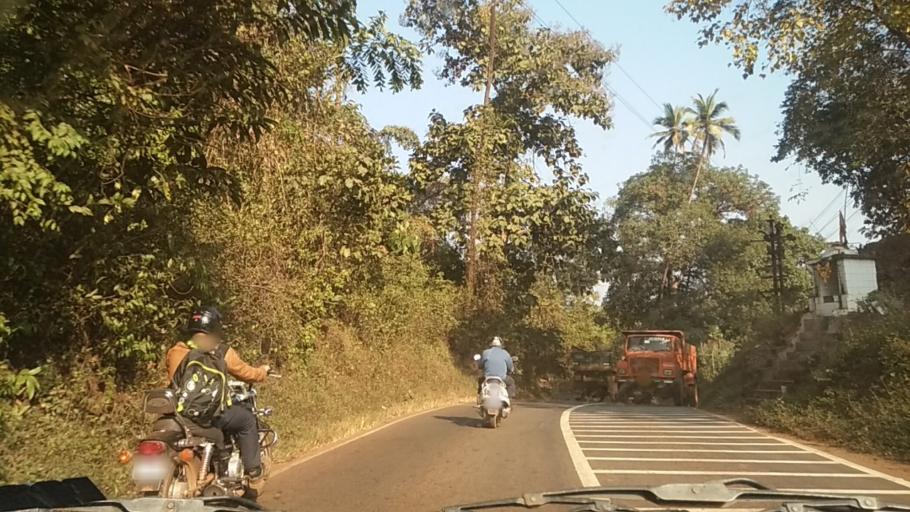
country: IN
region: Goa
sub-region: South Goa
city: Sanvordem
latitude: 15.2761
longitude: 74.1201
